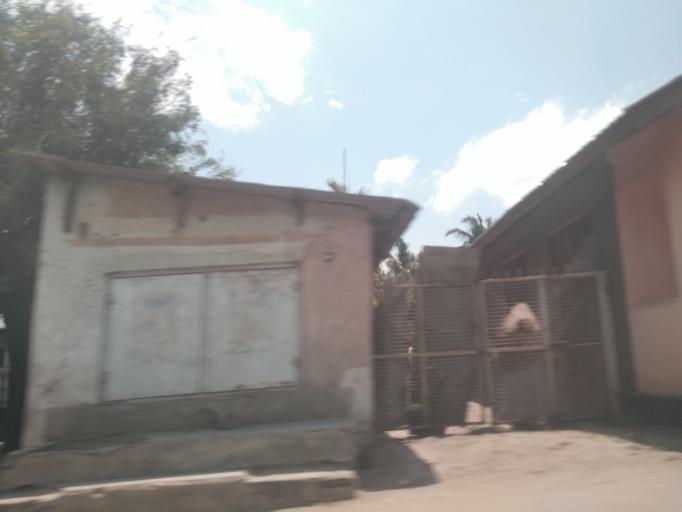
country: TZ
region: Dar es Salaam
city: Dar es Salaam
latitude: -6.8875
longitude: 39.2706
